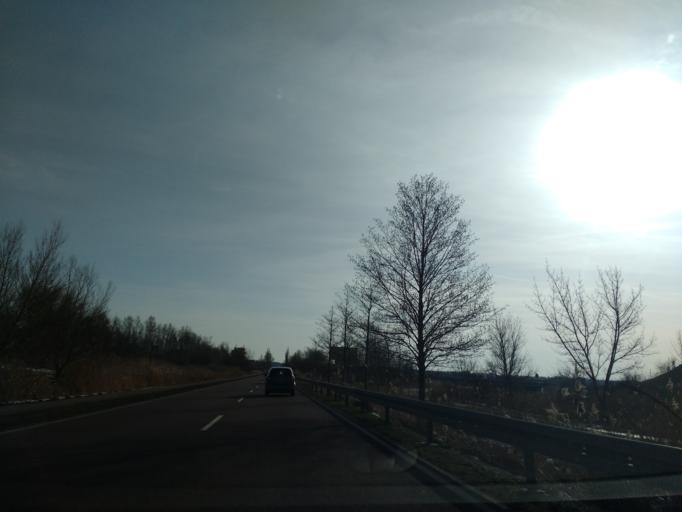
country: DE
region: Saxony-Anhalt
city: Sennewitz
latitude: 51.5327
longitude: 11.9559
